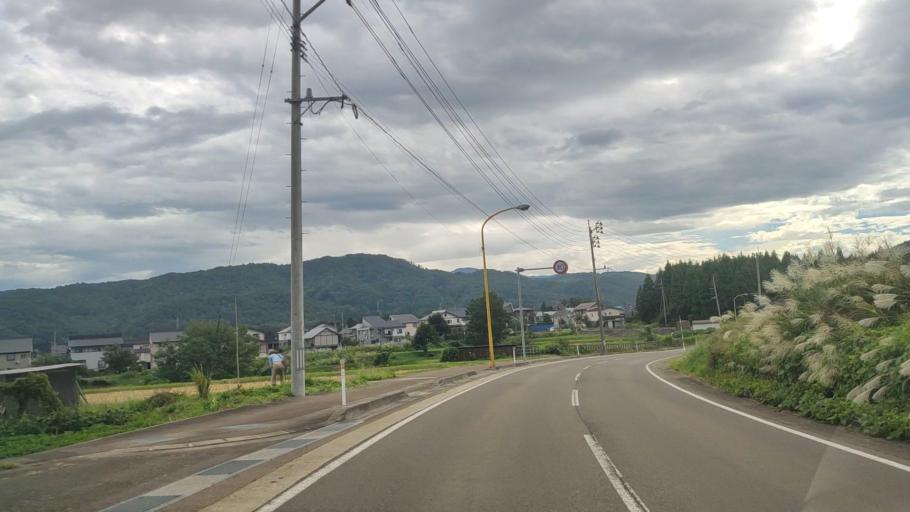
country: JP
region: Niigata
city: Arai
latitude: 37.0117
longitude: 138.2560
